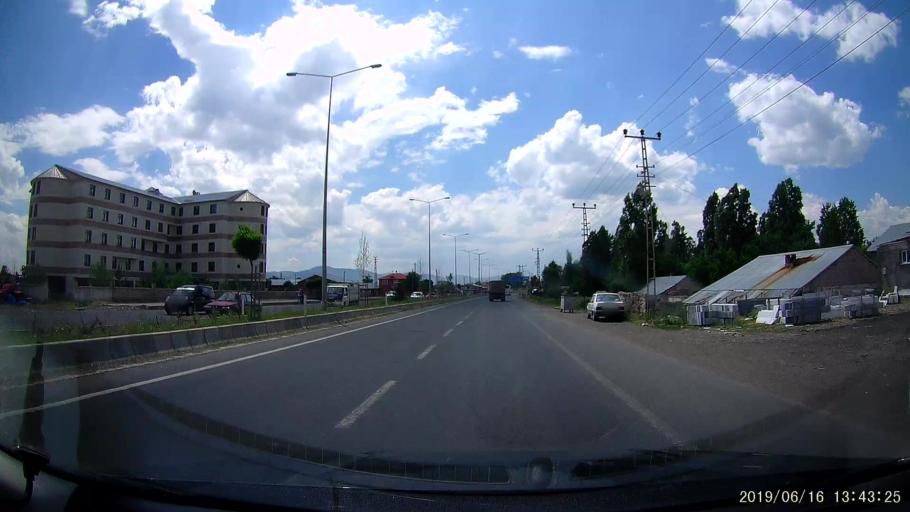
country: TR
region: Agri
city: Agri
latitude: 39.7080
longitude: 43.0554
